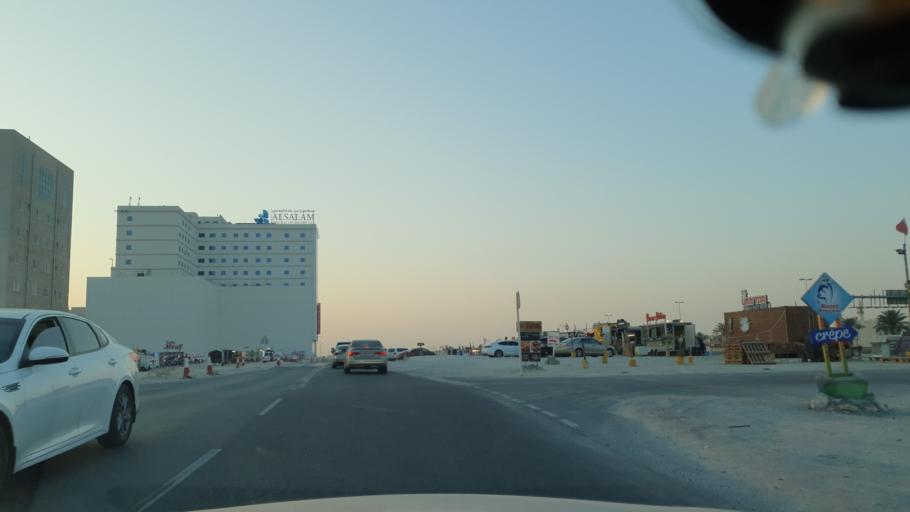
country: BH
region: Northern
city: Ar Rifa'
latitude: 26.1528
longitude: 50.5707
